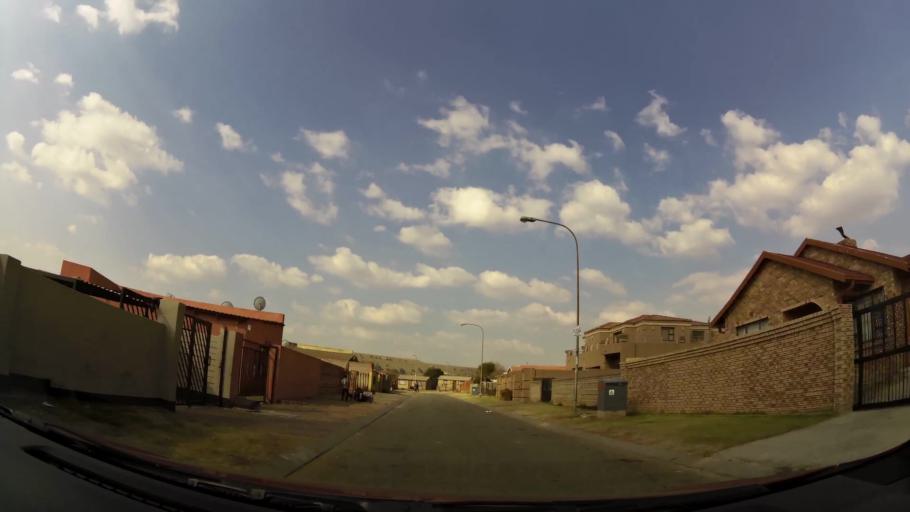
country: ZA
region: Gauteng
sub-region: City of Johannesburg Metropolitan Municipality
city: Soweto
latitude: -26.2359
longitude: 27.9500
